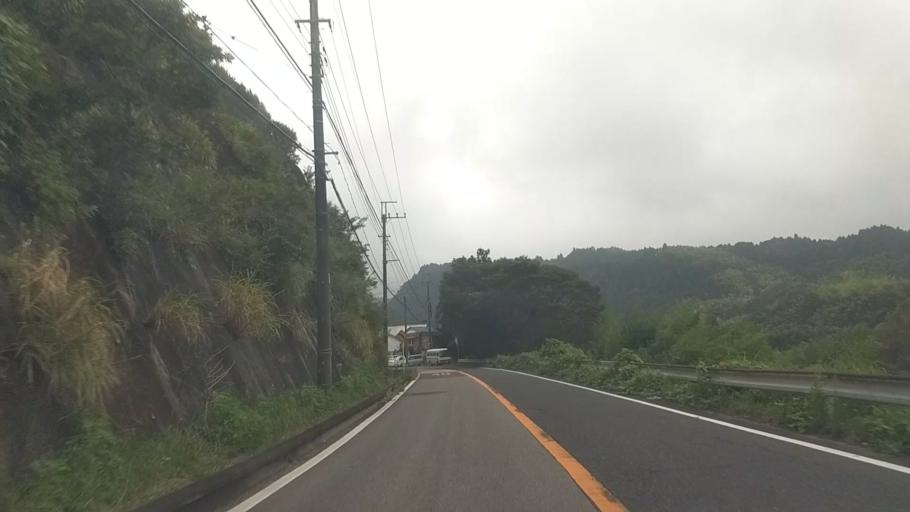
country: JP
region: Chiba
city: Katsuura
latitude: 35.2425
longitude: 140.2380
